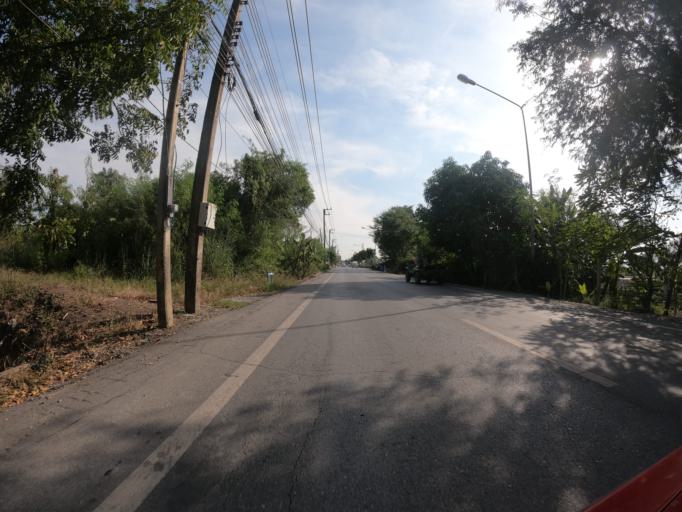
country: TH
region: Pathum Thani
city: Thanyaburi
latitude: 13.9924
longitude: 100.7302
